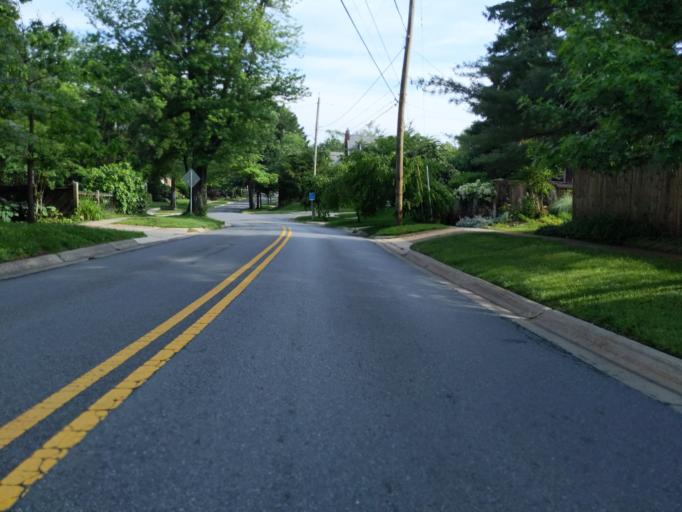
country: US
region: Maryland
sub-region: Montgomery County
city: Forest Glen
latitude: 39.0069
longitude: -77.0431
